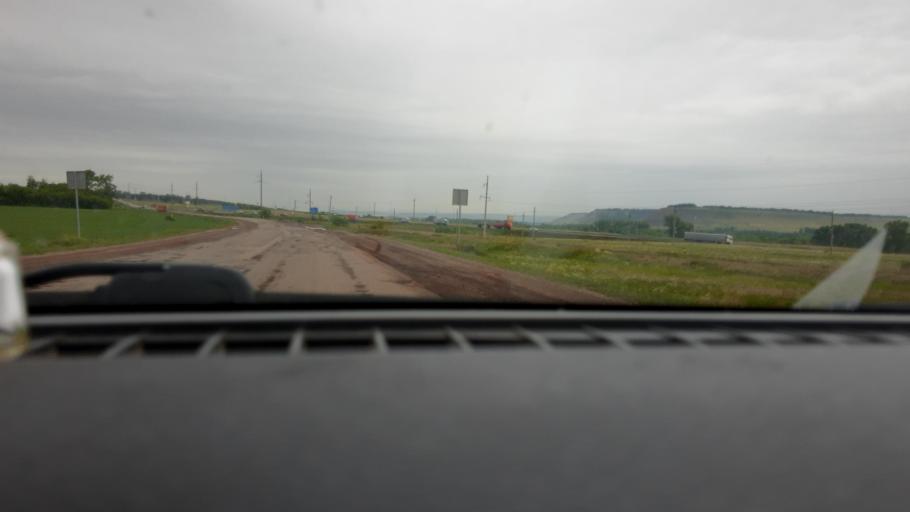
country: RU
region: Bashkortostan
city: Subkhankulovo
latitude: 54.4825
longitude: 53.9116
